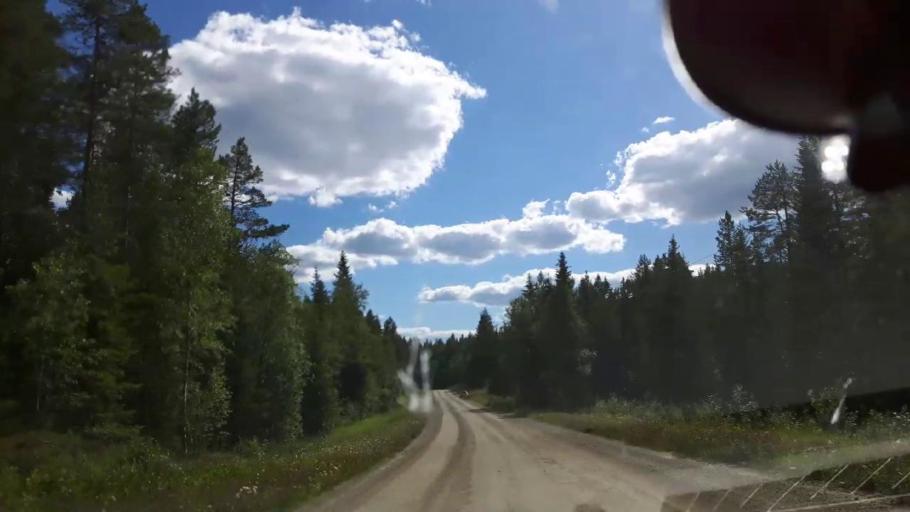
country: SE
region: Vaesternorrland
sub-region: Ange Kommun
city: Ange
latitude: 62.7263
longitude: 15.6386
